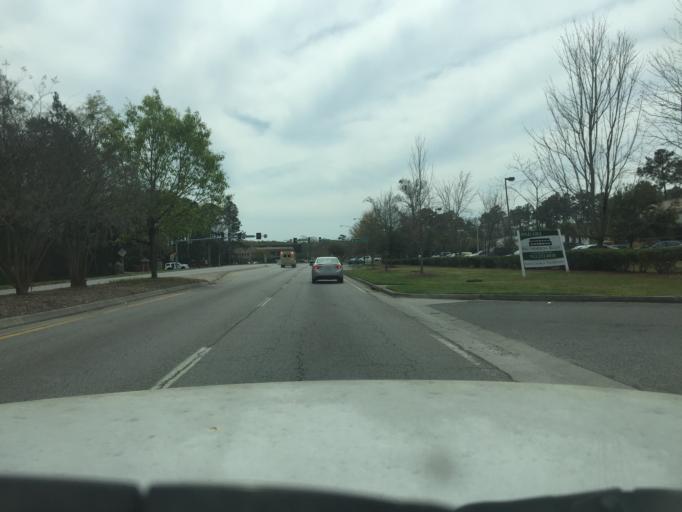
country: US
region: Georgia
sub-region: Chatham County
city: Garden City
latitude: 32.0671
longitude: -81.1605
